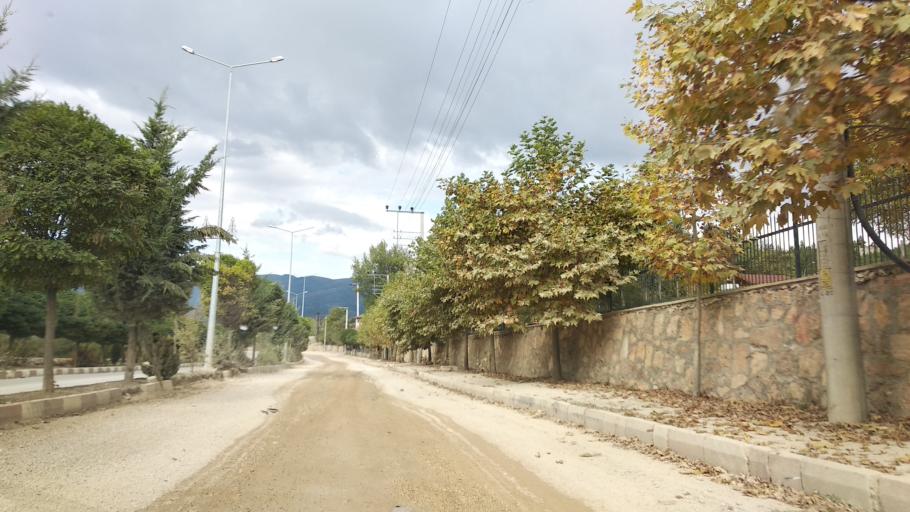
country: TR
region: Bolu
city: Mudurnu
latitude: 40.4786
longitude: 31.2103
